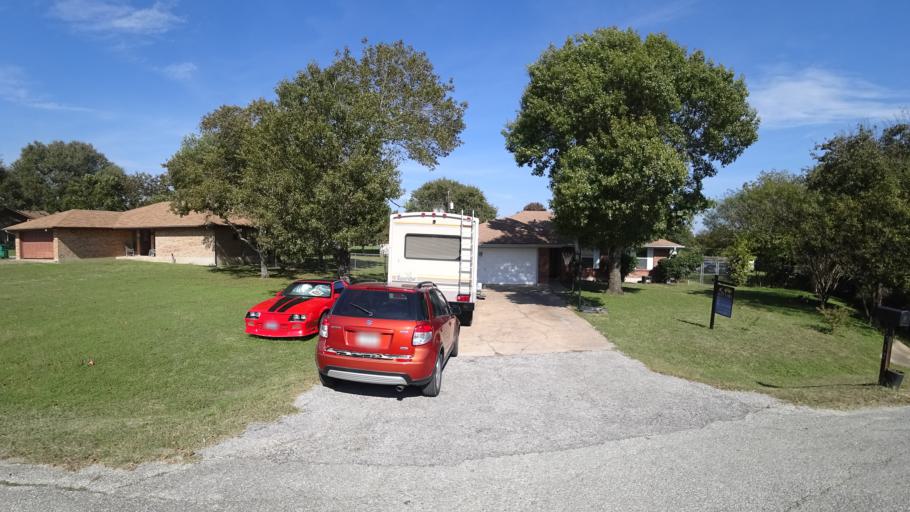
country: US
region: Texas
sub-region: Travis County
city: Pflugerville
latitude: 30.4186
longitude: -97.6256
